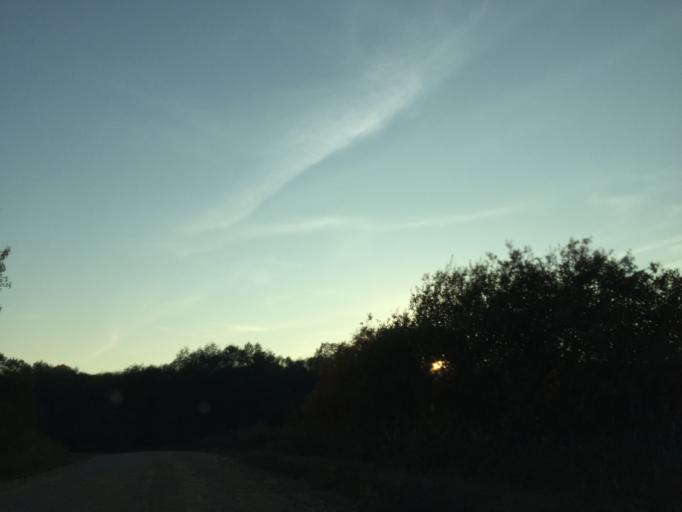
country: LV
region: Vainode
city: Vainode
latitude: 56.4954
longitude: 21.7951
